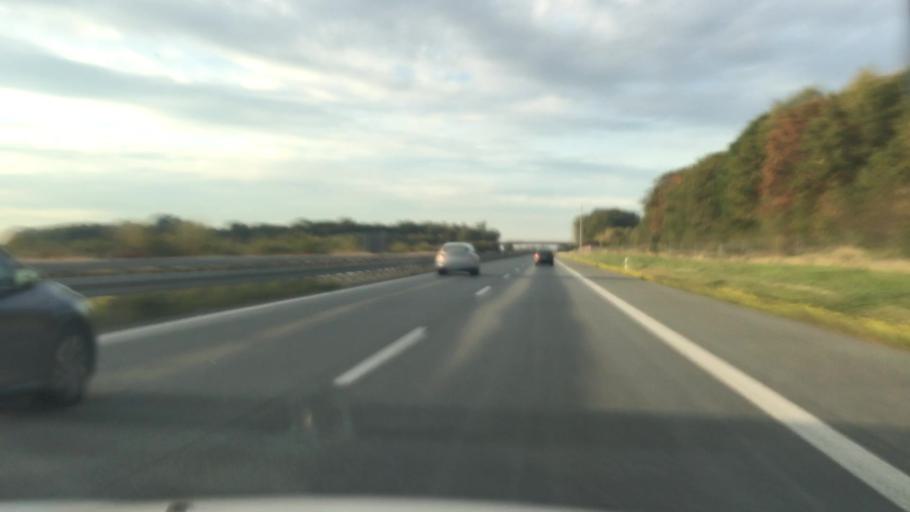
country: DE
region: Saxony
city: Schonfeld
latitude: 51.3172
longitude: 13.7232
